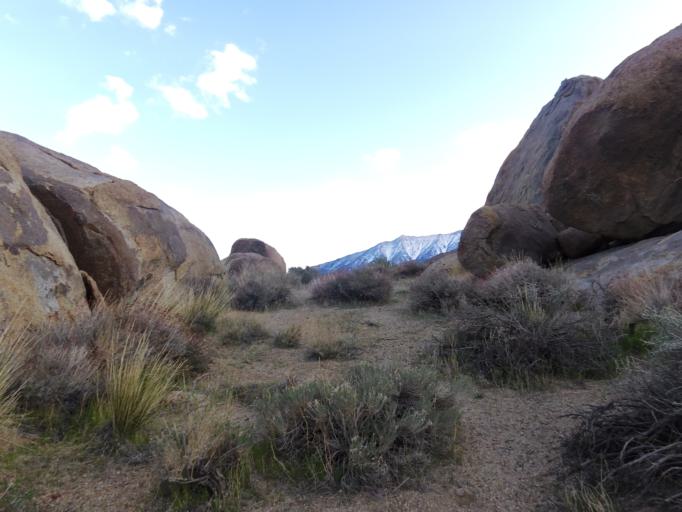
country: US
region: California
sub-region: Inyo County
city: Lone Pine
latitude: 36.6003
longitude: -118.1182
